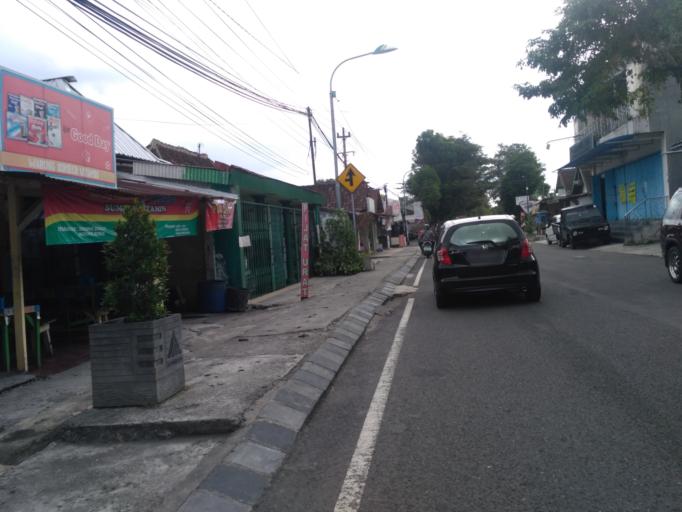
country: ID
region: Daerah Istimewa Yogyakarta
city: Melati
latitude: -7.7408
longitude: 110.3622
